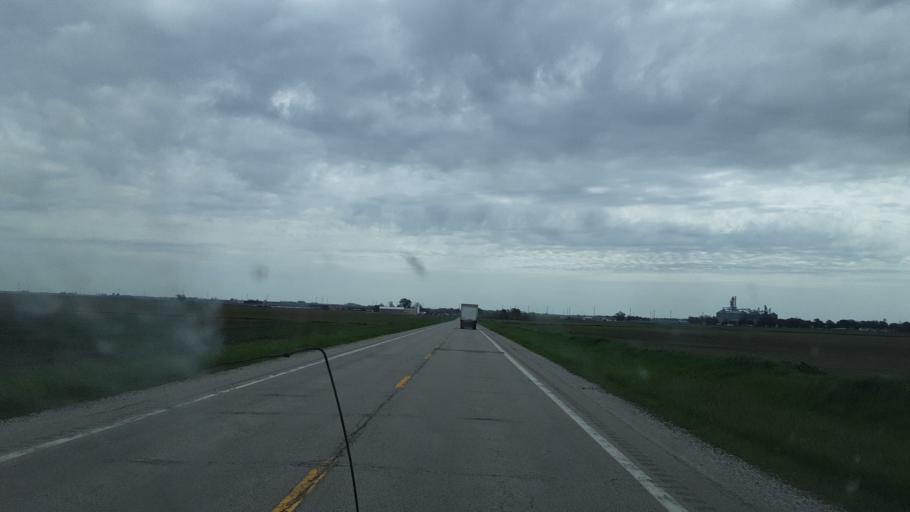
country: US
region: Illinois
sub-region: Tazewell County
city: Delavan
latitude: 40.3071
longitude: -89.5080
